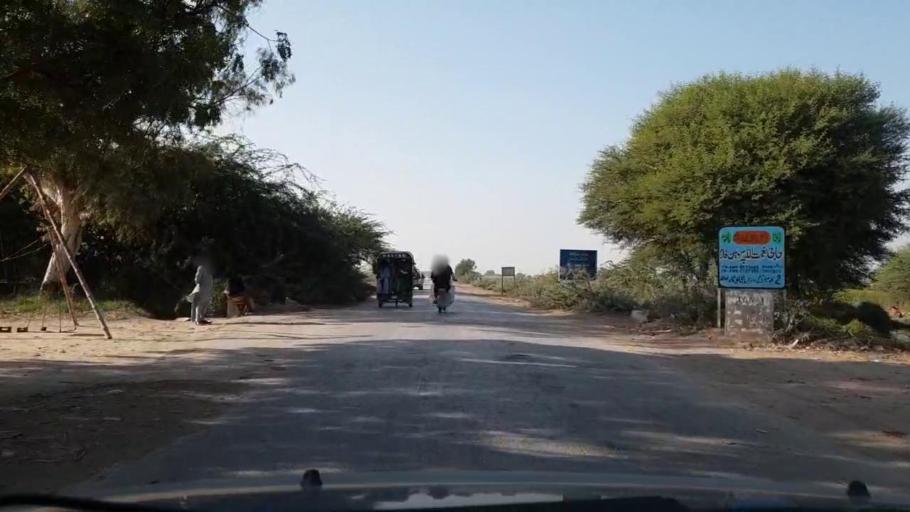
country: PK
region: Sindh
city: Tando Ghulam Ali
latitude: 25.1412
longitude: 68.8716
